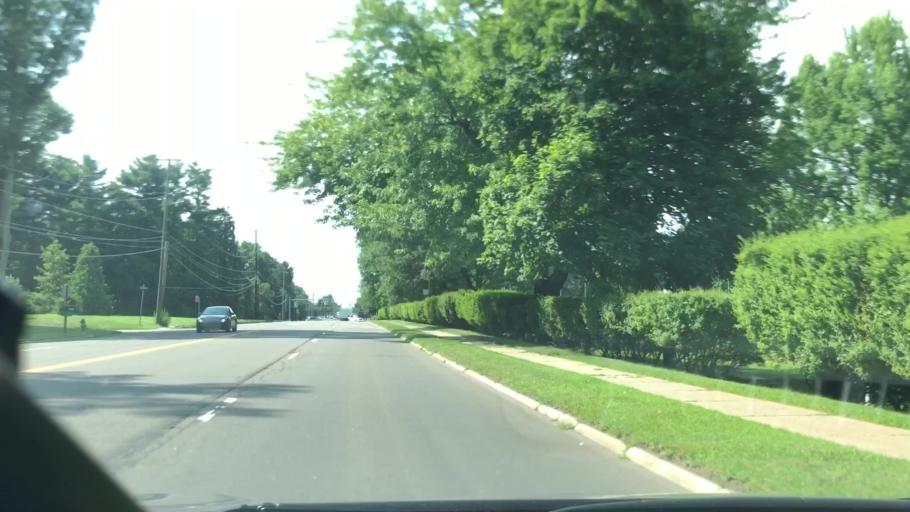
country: US
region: Ohio
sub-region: Summit County
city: Fairlawn
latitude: 41.1210
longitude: -81.5949
